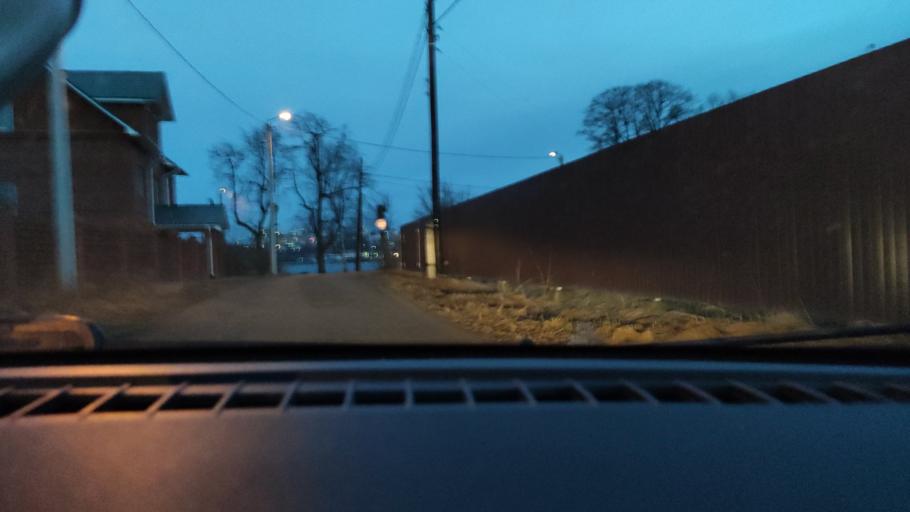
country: RU
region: Perm
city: Perm
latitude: 58.0329
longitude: 56.2495
